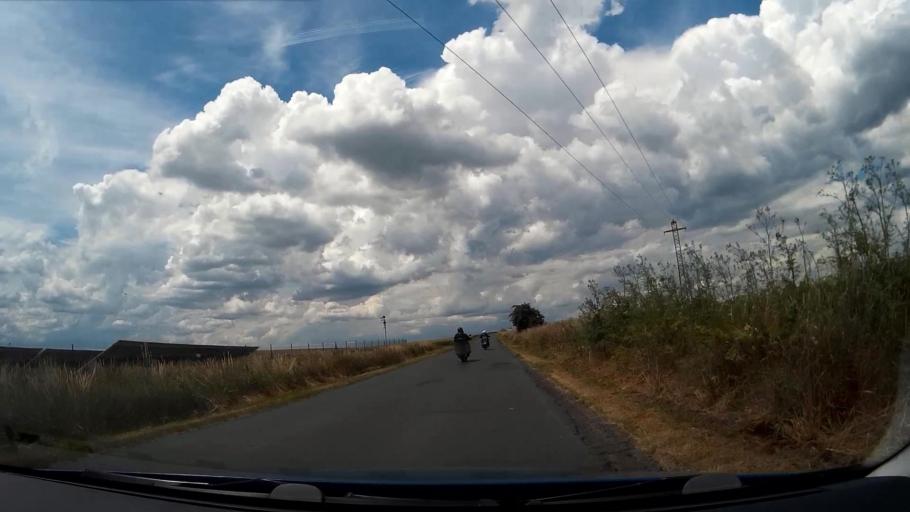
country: CZ
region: South Moravian
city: Orechov
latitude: 49.0856
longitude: 16.5365
